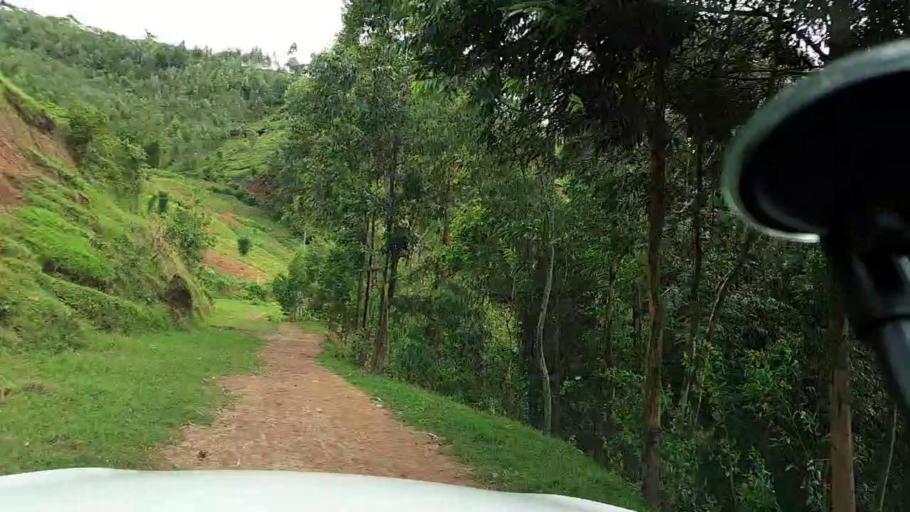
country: RW
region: Southern Province
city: Gitarama
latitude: -2.0730
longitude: 29.6438
